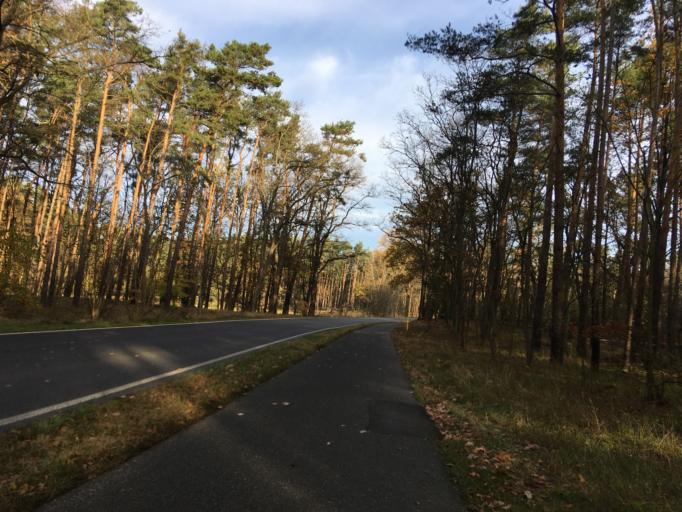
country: DE
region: Brandenburg
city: Luebben
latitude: 51.9562
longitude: 13.8818
